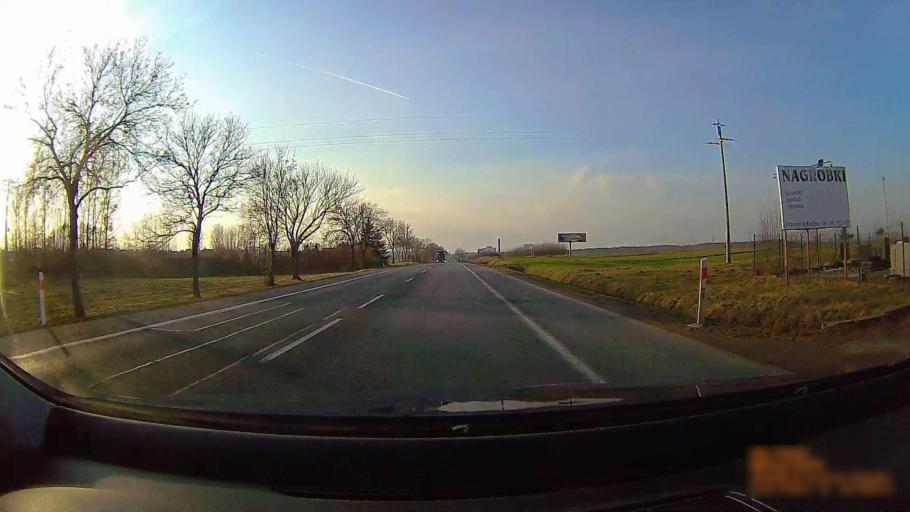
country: PL
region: Greater Poland Voivodeship
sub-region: Konin
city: Konin
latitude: 52.1914
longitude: 18.3292
